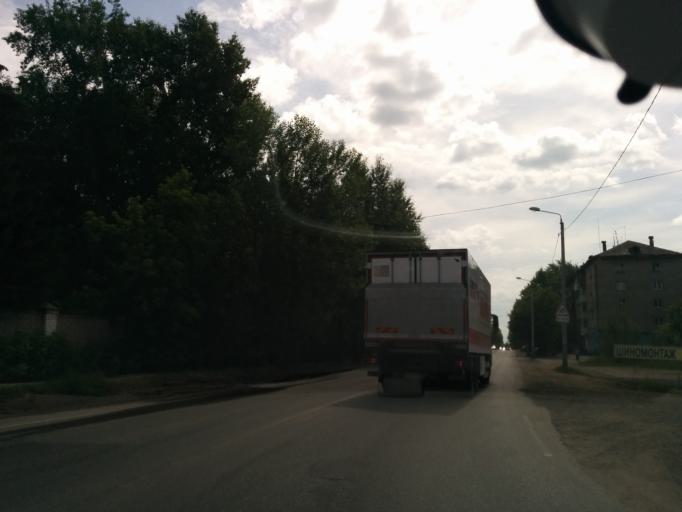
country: RU
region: Perm
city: Overyata
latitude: 58.0202
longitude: 55.9746
